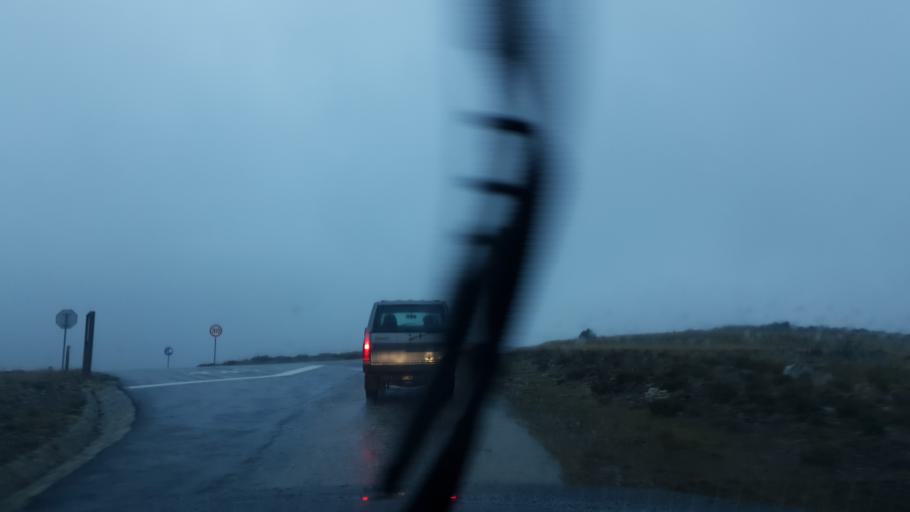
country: PT
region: Viseu
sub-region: Sao Pedro do Sul
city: Sao Pedro do Sul
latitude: 40.8299
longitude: -8.1243
